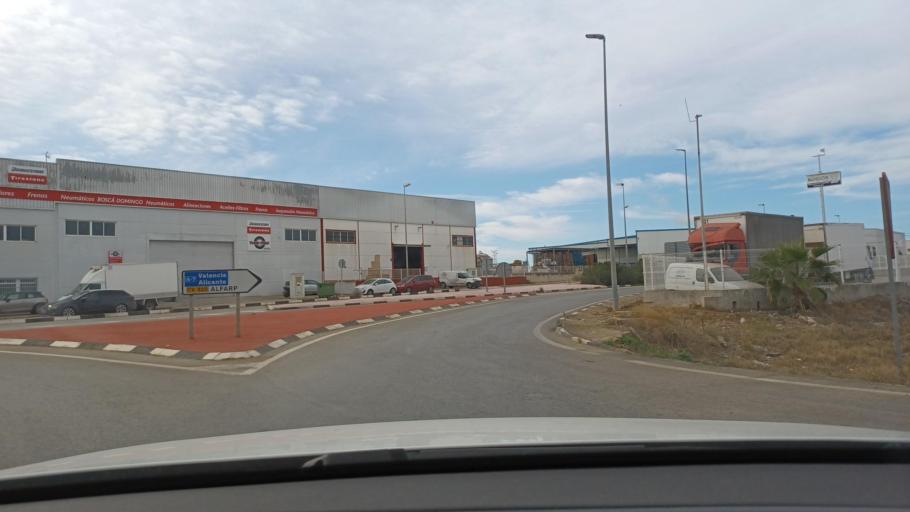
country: ES
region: Valencia
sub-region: Provincia de Valencia
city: Benifaio
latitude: 39.2886
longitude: -0.4422
